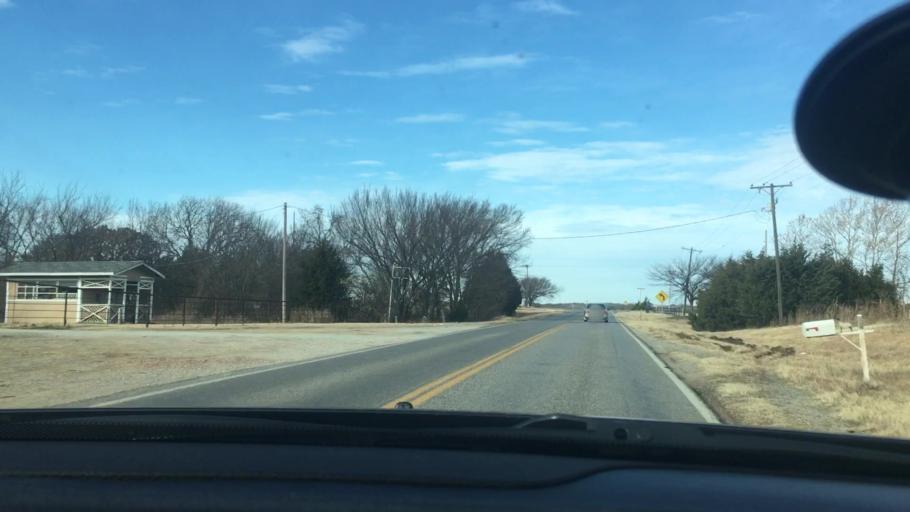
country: US
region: Oklahoma
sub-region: Seminole County
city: Konawa
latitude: 34.9484
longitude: -96.7381
